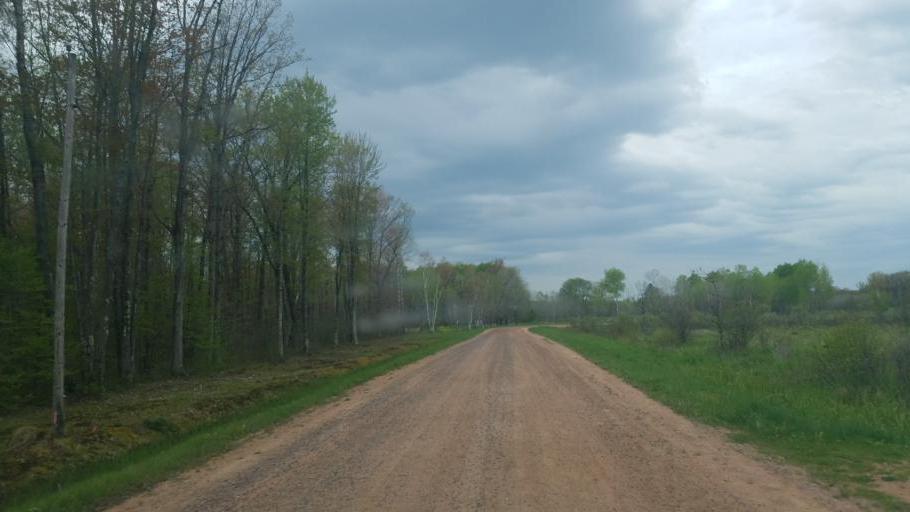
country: US
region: Wisconsin
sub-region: Wood County
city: Marshfield
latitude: 44.4389
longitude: -90.2365
